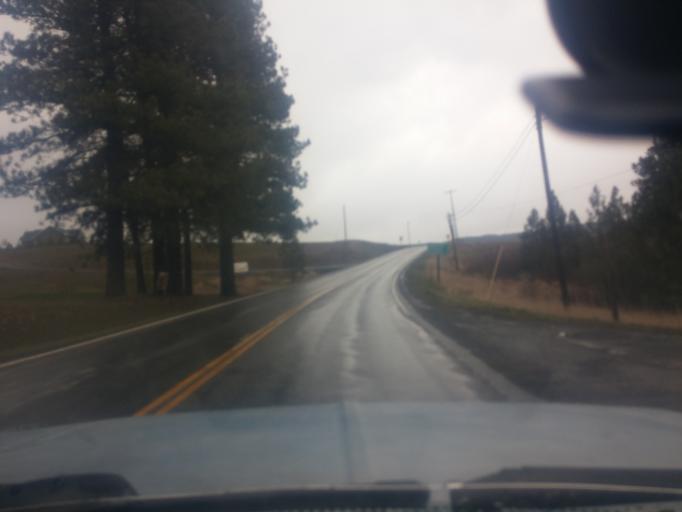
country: US
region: Idaho
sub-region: Latah County
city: Moscow
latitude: 46.9214
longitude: -116.8889
